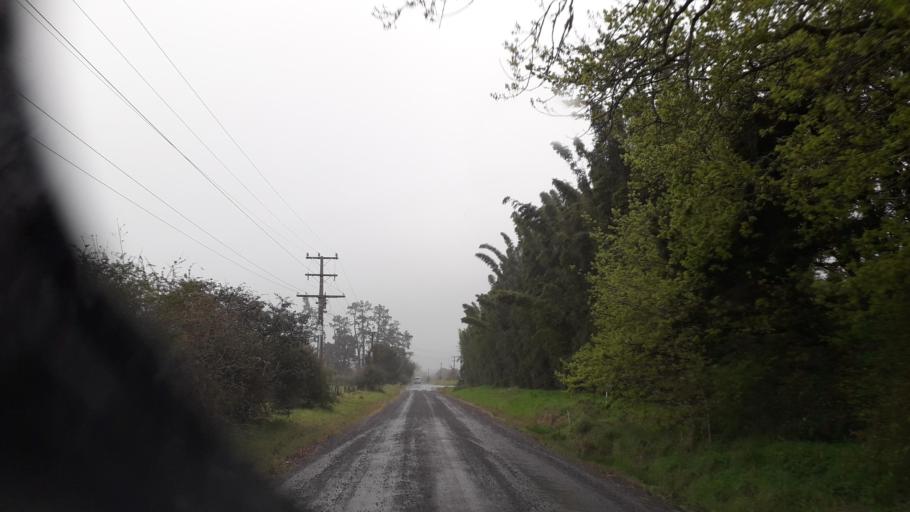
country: NZ
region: Northland
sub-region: Far North District
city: Waimate North
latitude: -35.4974
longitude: 173.6992
